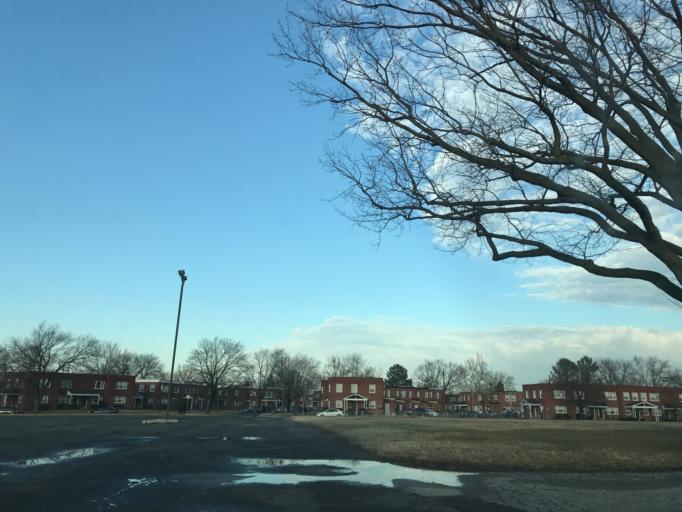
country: US
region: Maryland
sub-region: Baltimore County
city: Dundalk
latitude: 39.2684
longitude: -76.4919
